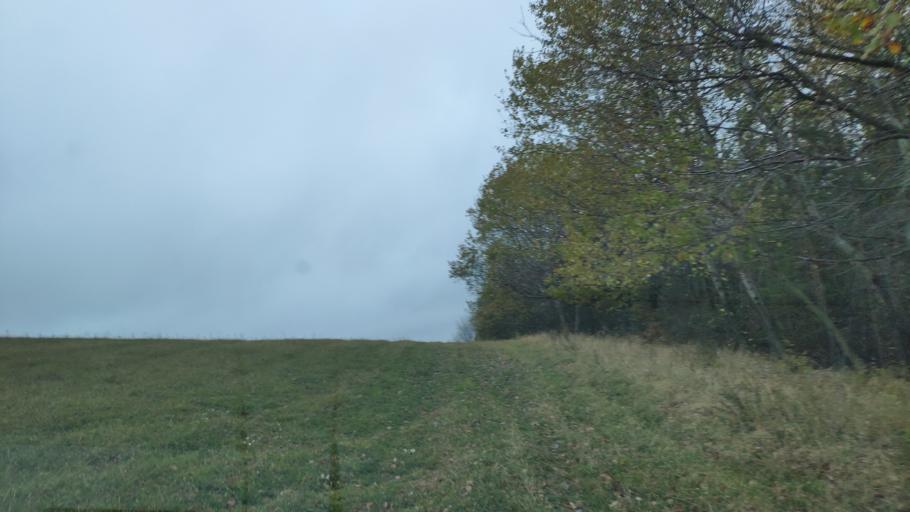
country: SK
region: Presovsky
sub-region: Okres Presov
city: Presov
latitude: 48.9359
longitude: 21.1200
